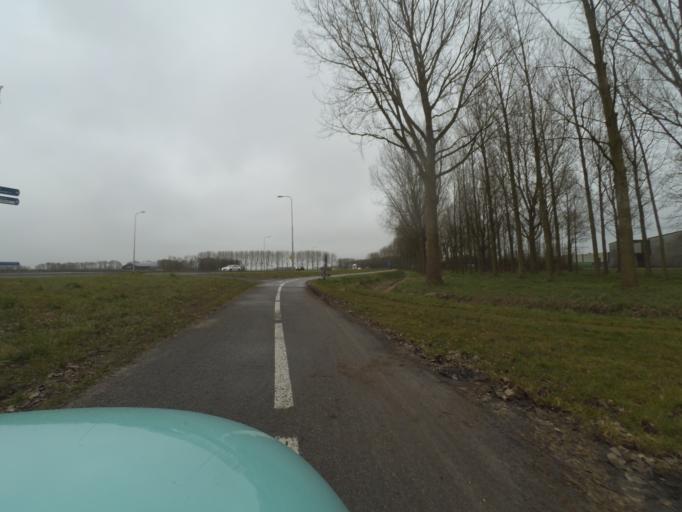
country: NL
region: Flevoland
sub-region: Gemeente Dronten
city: Dronten
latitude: 52.5392
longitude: 5.7263
